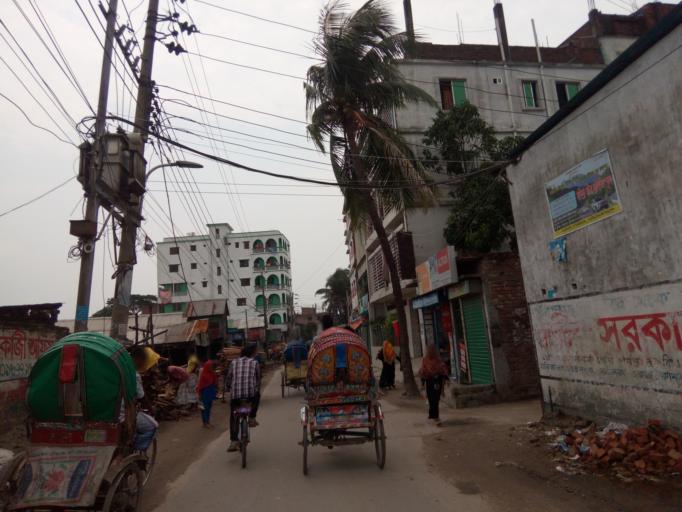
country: BD
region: Dhaka
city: Azimpur
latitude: 23.7105
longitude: 90.3646
